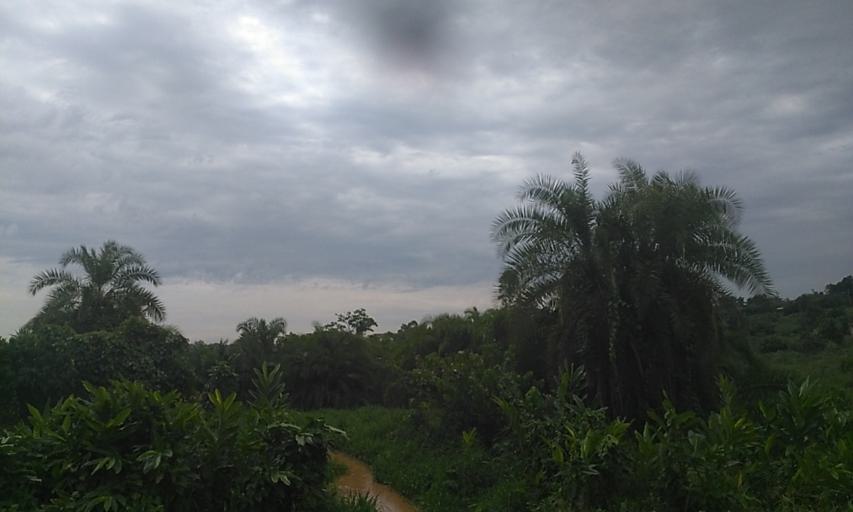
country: UG
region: Central Region
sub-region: Wakiso District
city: Bweyogerere
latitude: 0.3978
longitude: 32.6730
